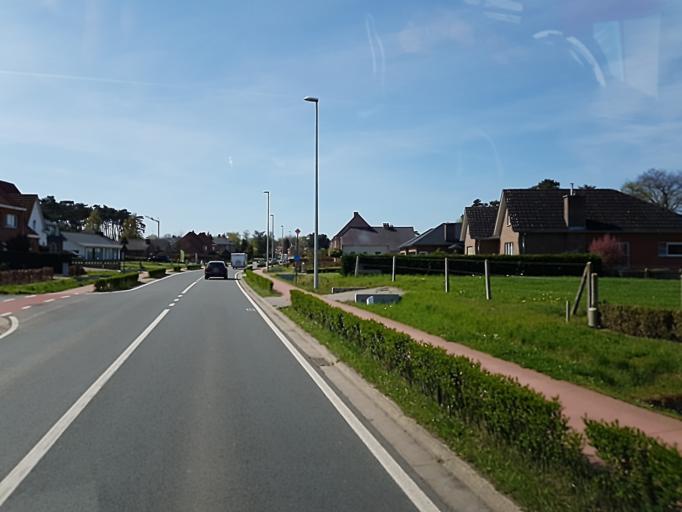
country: BE
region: Flanders
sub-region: Provincie Antwerpen
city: Herselt
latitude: 51.0627
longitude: 4.8904
